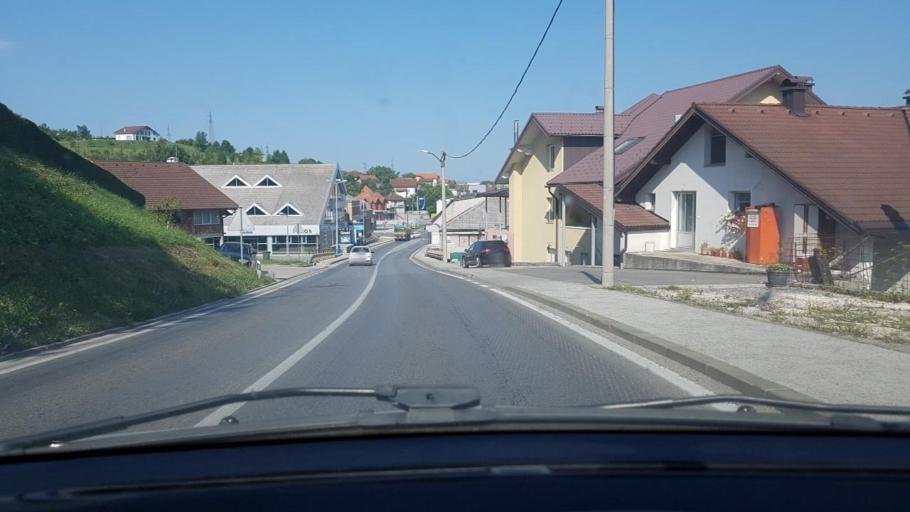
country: BA
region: Federation of Bosnia and Herzegovina
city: Cazin
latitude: 44.9651
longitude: 15.9253
